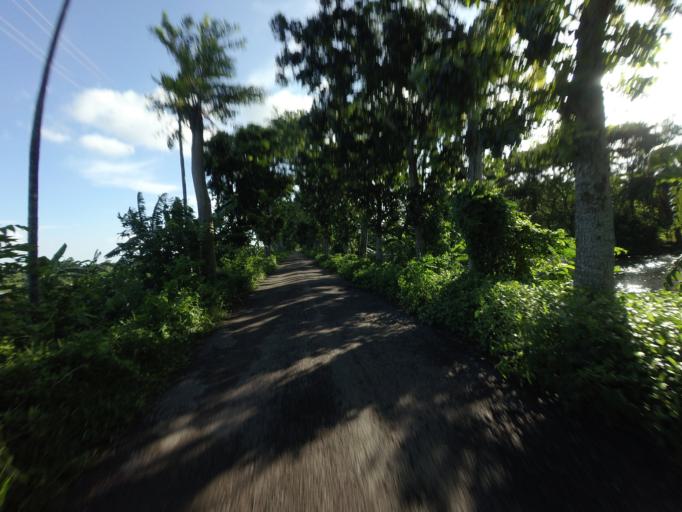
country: BD
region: Khulna
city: Bhatpara Abhaynagar
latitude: 22.9489
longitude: 89.5448
